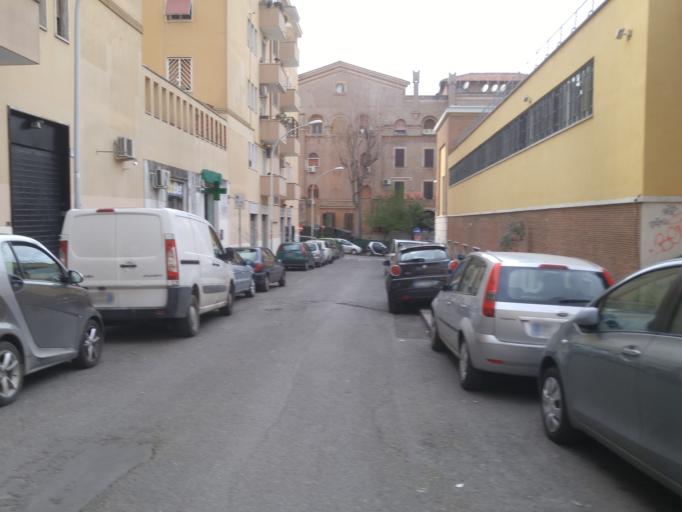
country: IT
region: Latium
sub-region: Citta metropolitana di Roma Capitale
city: Rome
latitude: 41.8615
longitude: 12.4870
